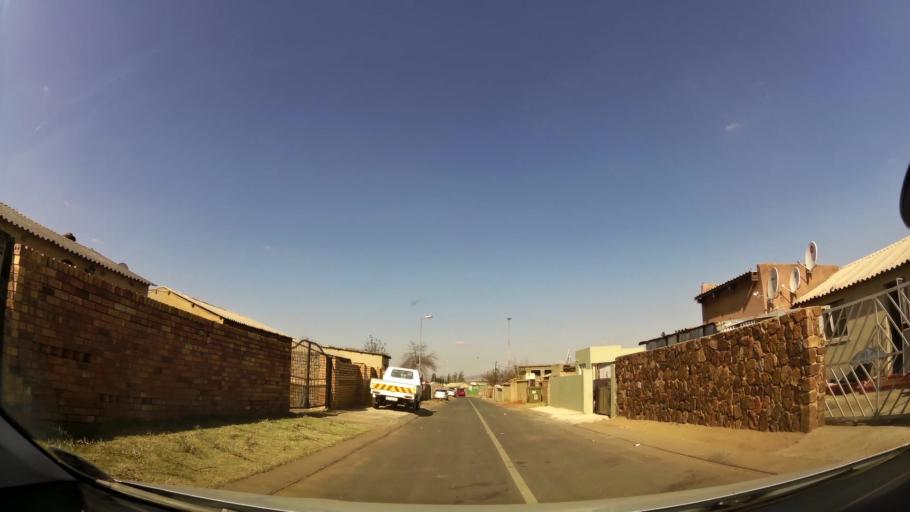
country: ZA
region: Gauteng
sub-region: City of Johannesburg Metropolitan Municipality
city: Soweto
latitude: -26.2830
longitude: 27.8609
